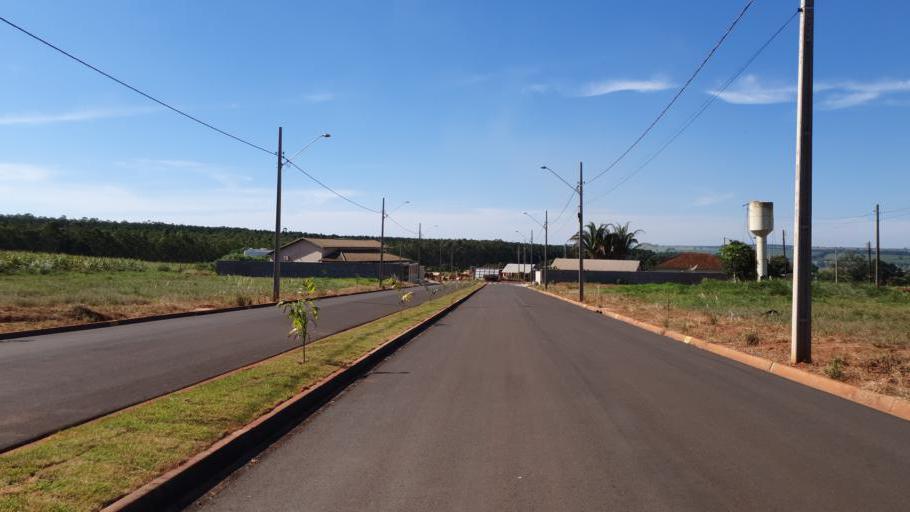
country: BR
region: Sao Paulo
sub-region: Paraguacu Paulista
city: Paraguacu Paulista
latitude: -22.3996
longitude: -50.5796
